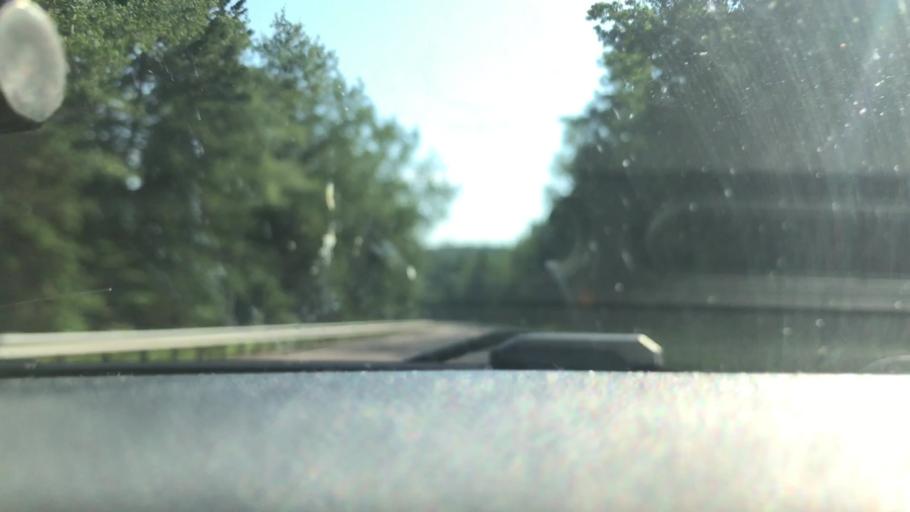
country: US
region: Minnesota
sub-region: Cook County
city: Grand Marais
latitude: 47.8407
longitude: -89.9691
